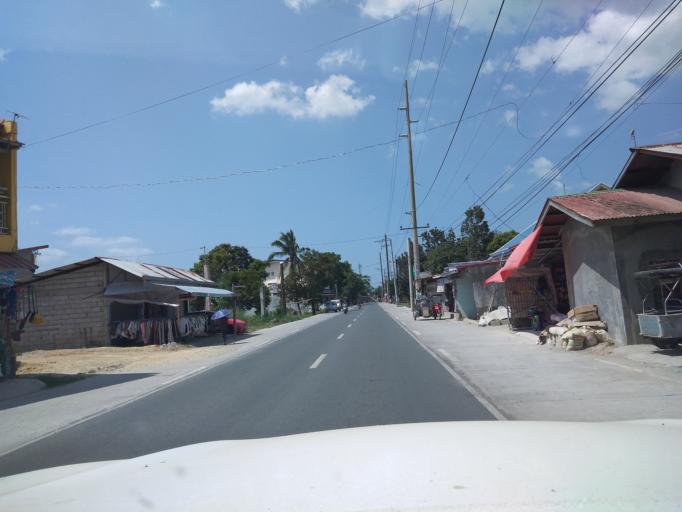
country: PH
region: Central Luzon
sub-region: Province of Pampanga
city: Bahay Pare
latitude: 15.0226
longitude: 120.8848
